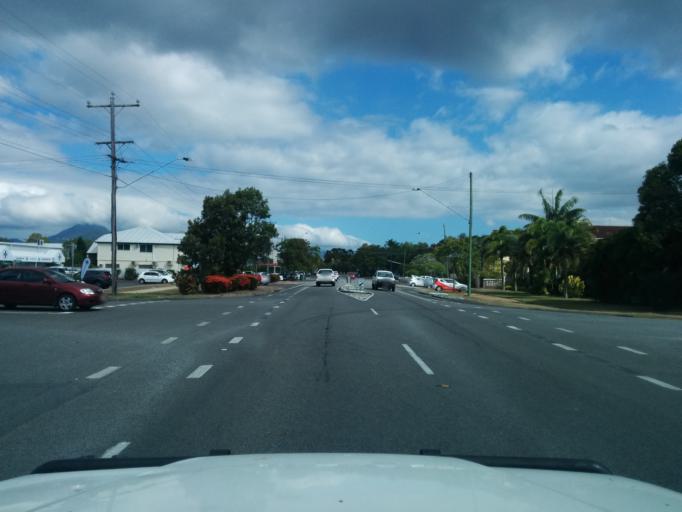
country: AU
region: Queensland
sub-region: Cairns
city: Cairns
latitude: -16.9124
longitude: 145.7627
